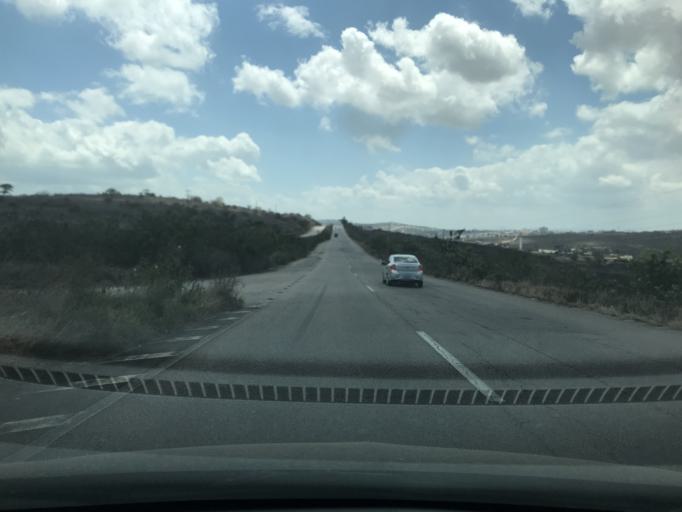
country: BR
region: Pernambuco
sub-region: Caruaru
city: Caruaru
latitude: -8.3052
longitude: -35.9332
